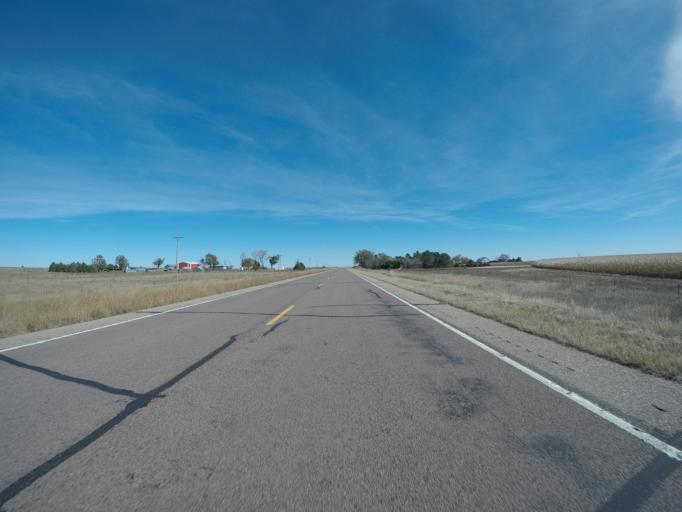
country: US
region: Colorado
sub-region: Kit Carson County
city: Burlington
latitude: 39.6581
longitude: -102.5398
